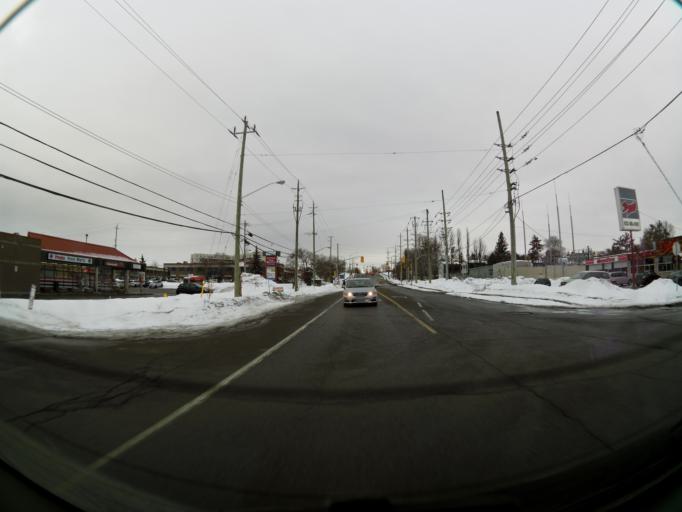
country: CA
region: Quebec
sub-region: Outaouais
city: Gatineau
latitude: 45.4527
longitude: -75.5897
